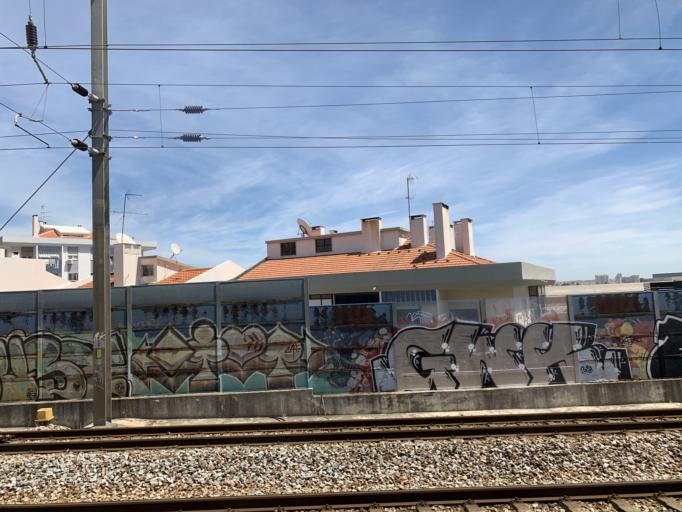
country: PT
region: Lisbon
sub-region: Amadora
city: Amadora
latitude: 38.7515
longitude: -9.2239
